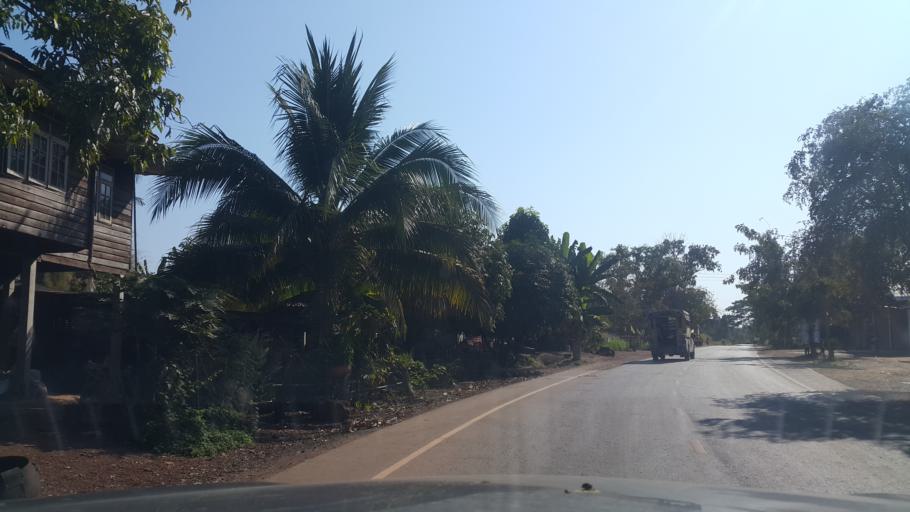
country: TH
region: Changwat Udon Thani
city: Ban Dung
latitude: 17.7037
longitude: 103.3878
